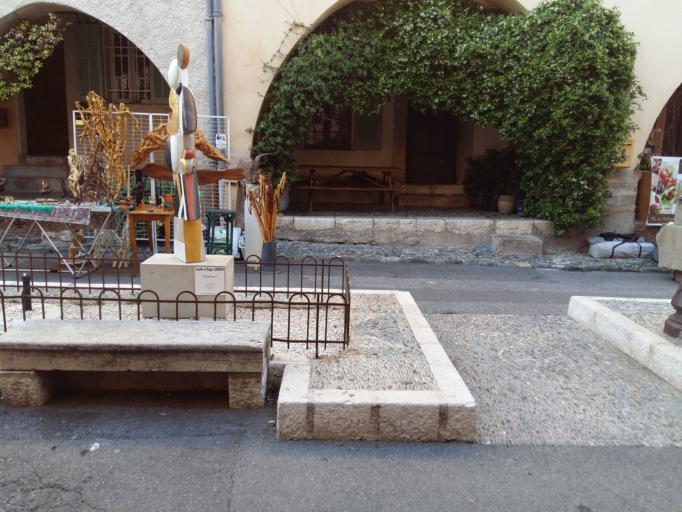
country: FR
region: Provence-Alpes-Cote d'Azur
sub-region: Departement des Alpes-Maritimes
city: Biot
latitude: 43.6269
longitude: 7.0993
